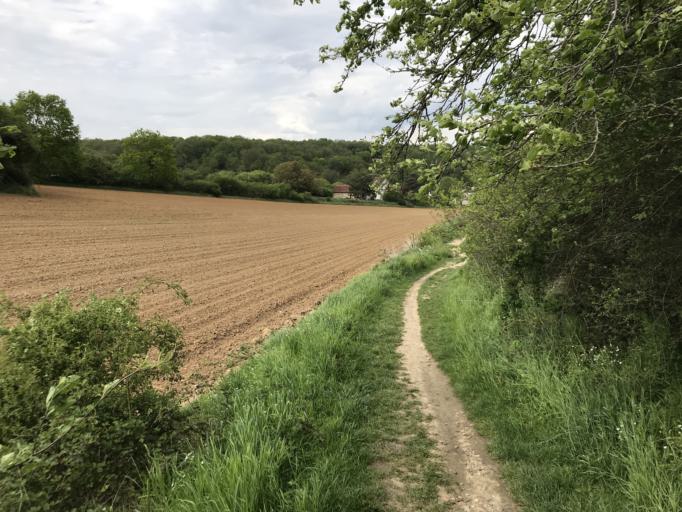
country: FR
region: Ile-de-France
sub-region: Departement de l'Essonne
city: Vauhallan
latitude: 48.7309
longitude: 2.1984
